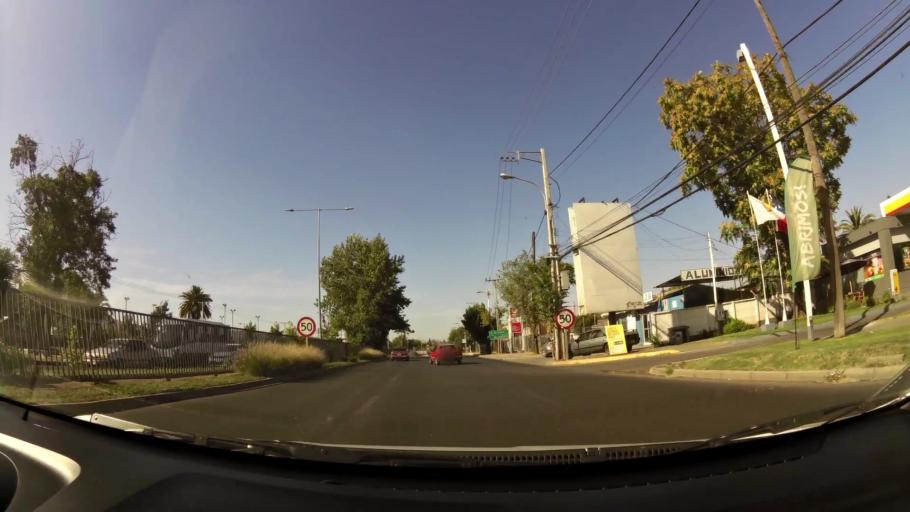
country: CL
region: Maule
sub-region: Provincia de Talca
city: Talca
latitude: -35.4313
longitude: -71.6771
